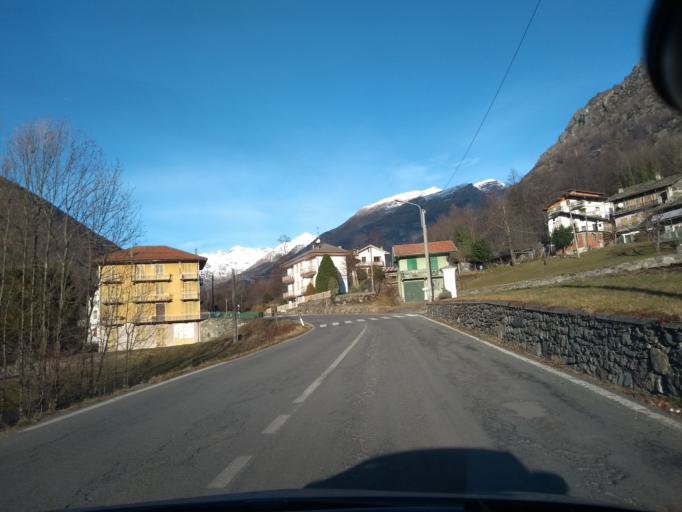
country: IT
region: Piedmont
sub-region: Provincia di Torino
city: Cantoira
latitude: 45.3463
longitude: 7.3744
